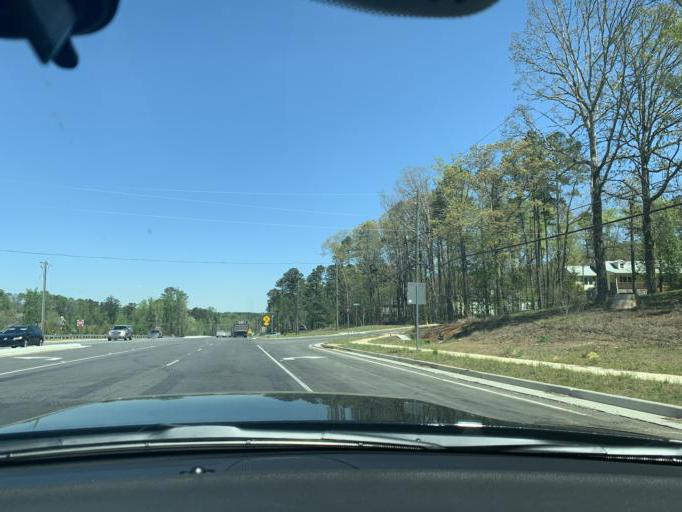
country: US
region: Georgia
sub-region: Forsyth County
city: Cumming
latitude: 34.2031
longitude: -84.1970
